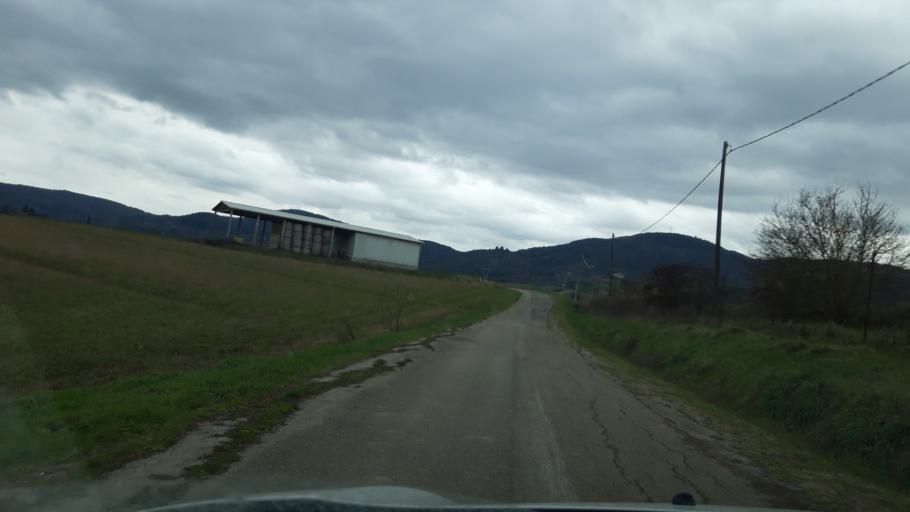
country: IT
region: Umbria
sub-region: Provincia di Perugia
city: Fontignano
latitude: 42.9937
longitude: 12.1805
